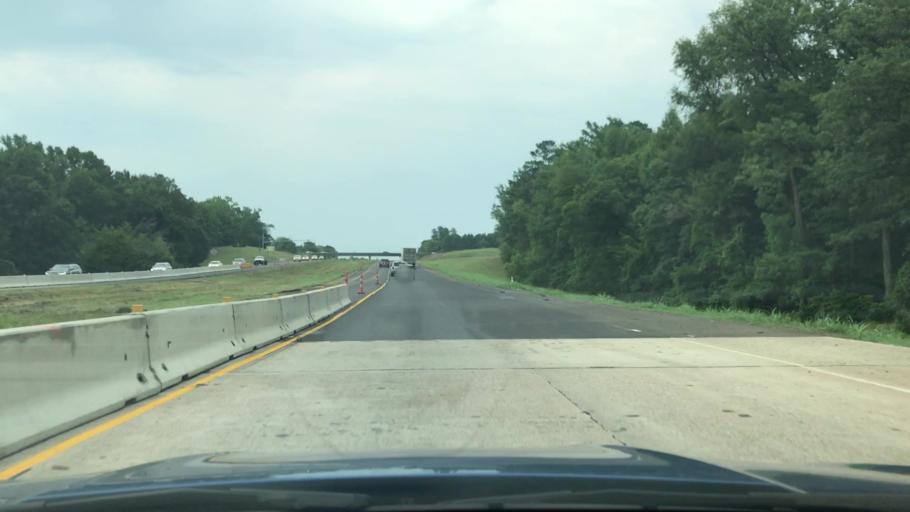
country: US
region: Louisiana
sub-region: Caddo Parish
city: Greenwood
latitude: 32.4516
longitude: -94.0174
